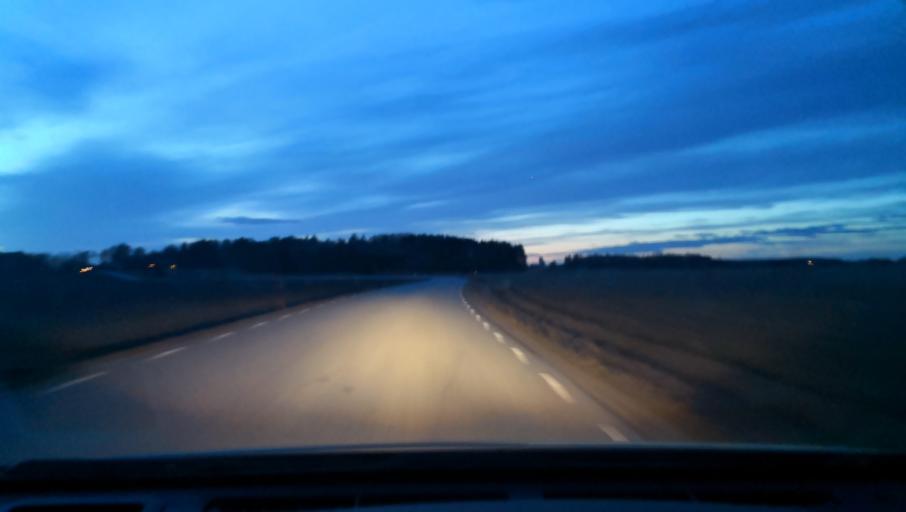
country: SE
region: Uppsala
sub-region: Enkopings Kommun
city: Grillby
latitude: 59.6054
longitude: 17.2943
